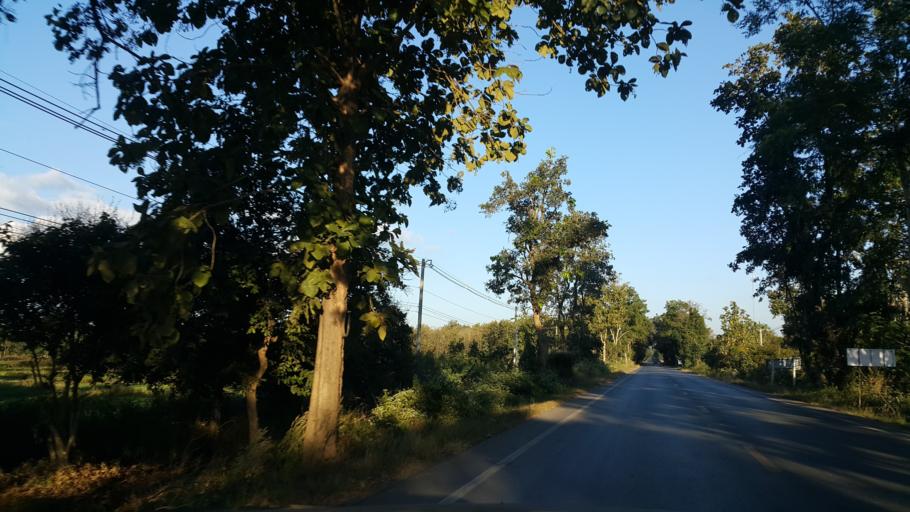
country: TH
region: Sukhothai
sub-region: Amphoe Si Satchanalai
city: Si Satchanalai
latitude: 17.5479
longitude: 99.8500
